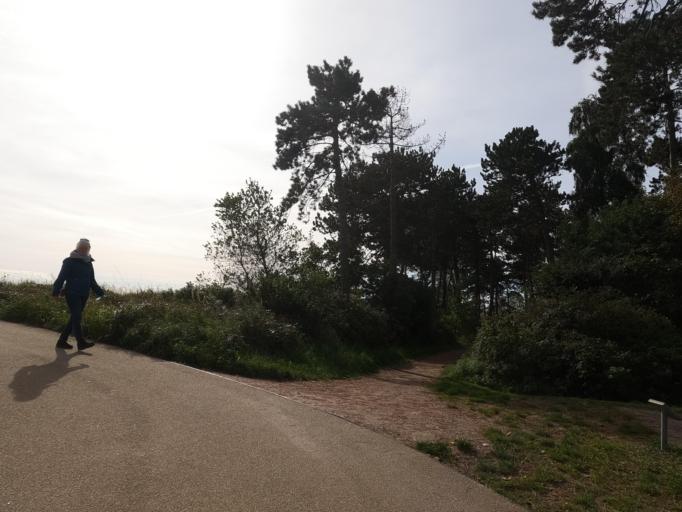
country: DE
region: Schleswig-Holstein
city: Kellenhusen
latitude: 54.1831
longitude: 11.0555
